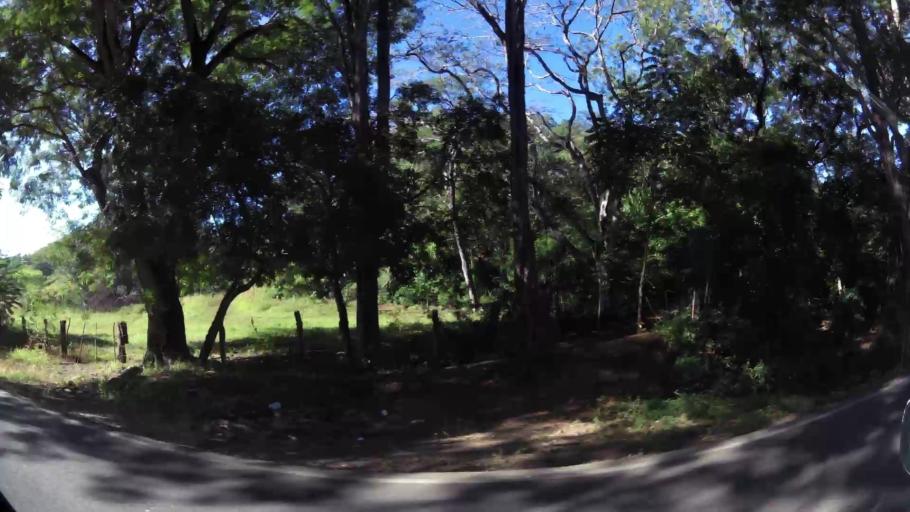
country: CR
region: Guanacaste
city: Belen
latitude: 10.3565
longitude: -85.7479
